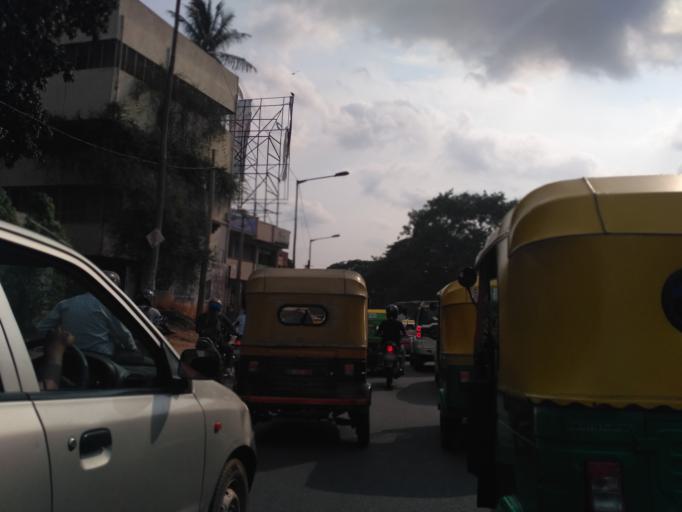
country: IN
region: Karnataka
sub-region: Bangalore Urban
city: Bangalore
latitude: 12.9564
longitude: 77.5472
